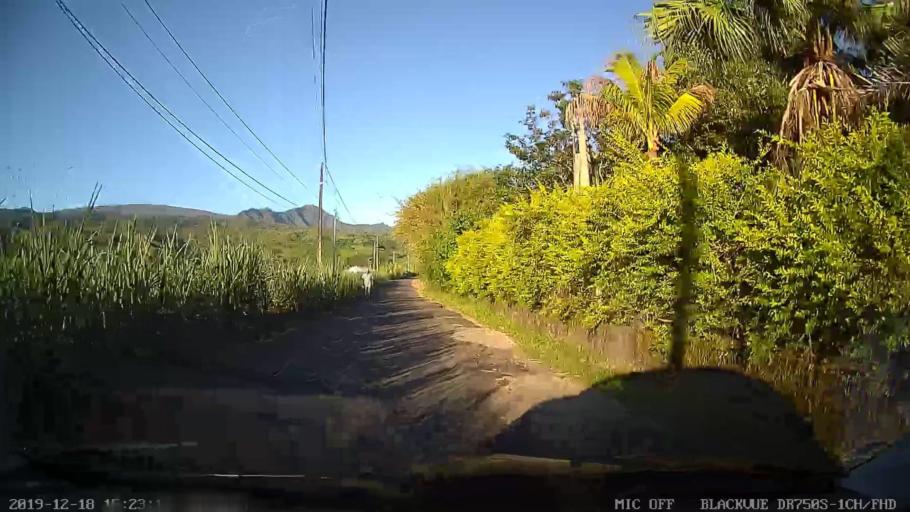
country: RE
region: Reunion
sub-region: Reunion
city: Bras-Panon
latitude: -20.9989
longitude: 55.6585
